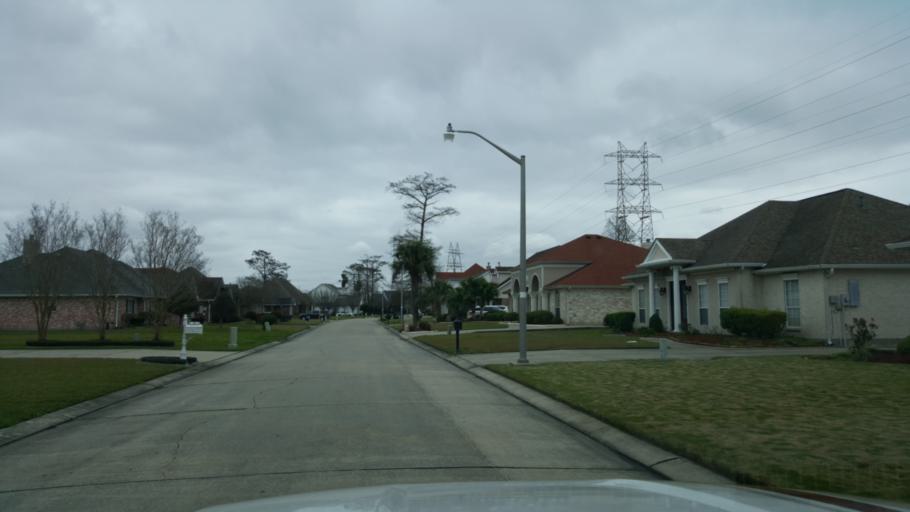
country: US
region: Louisiana
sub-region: Jefferson Parish
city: Harvey
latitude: 29.8810
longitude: -90.0822
